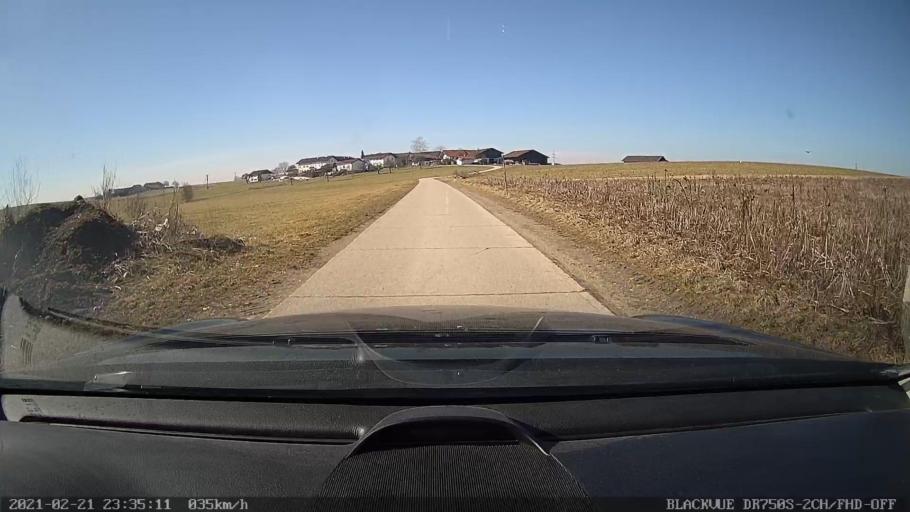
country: DE
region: Bavaria
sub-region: Upper Bavaria
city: Griesstatt
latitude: 48.0010
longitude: 12.2103
